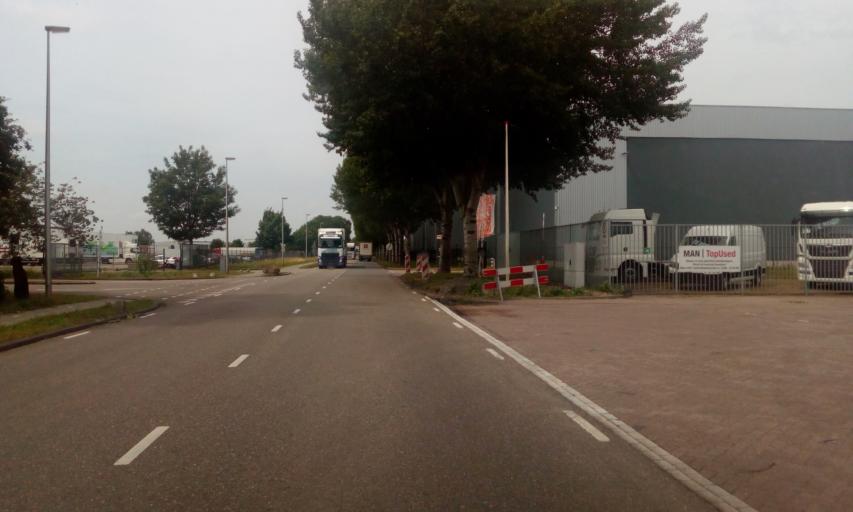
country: NL
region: South Holland
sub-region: Gemeente Waddinxveen
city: Waddinxveen
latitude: 52.0165
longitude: 4.6295
